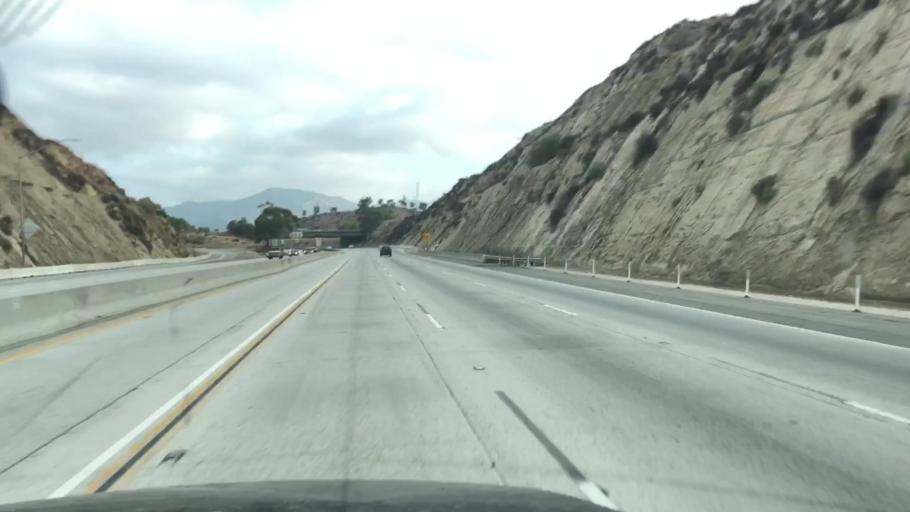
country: US
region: California
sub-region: Los Angeles County
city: San Fernando
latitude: 34.2856
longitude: -118.4681
